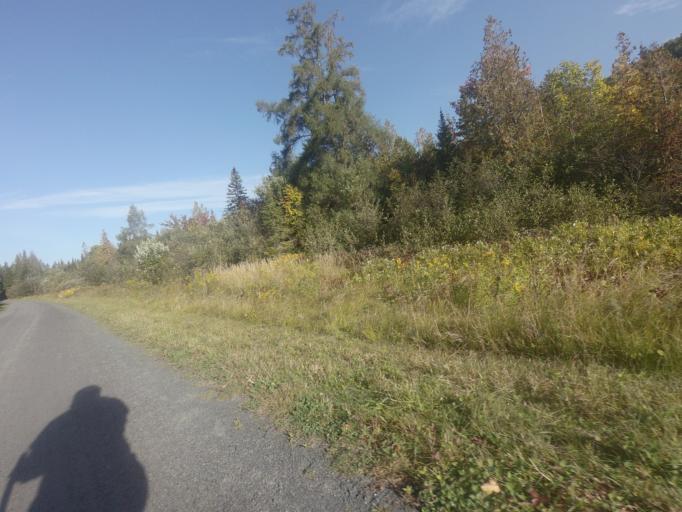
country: CA
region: Quebec
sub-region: Laurentides
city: Val-David
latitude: 46.0170
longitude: -74.1853
